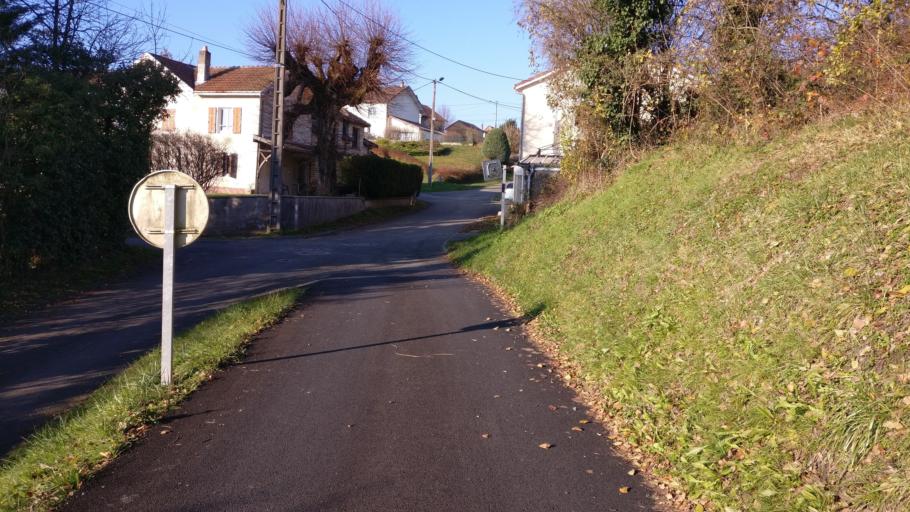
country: FR
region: Franche-Comte
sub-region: Departement du Doubs
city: Colombier-Fontaine
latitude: 47.4528
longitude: 6.6513
